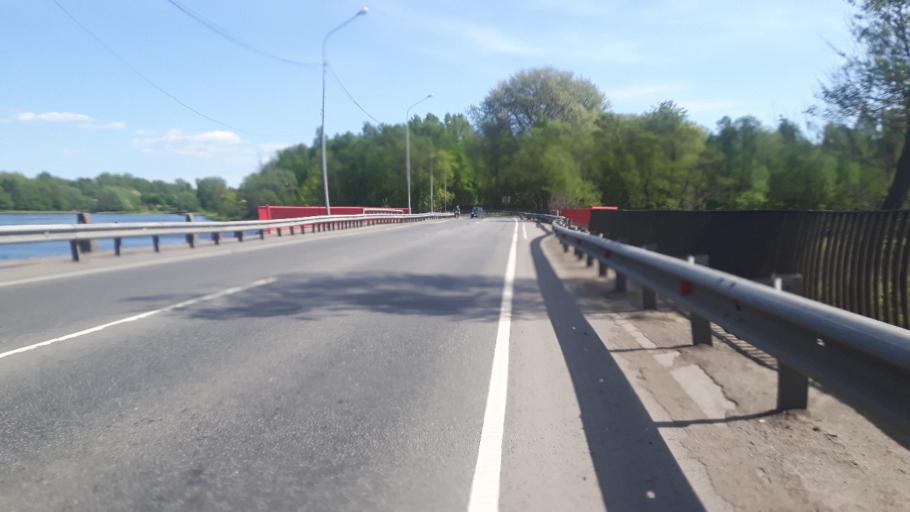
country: RU
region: Leningrad
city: Vyborg
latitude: 60.7255
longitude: 28.7076
